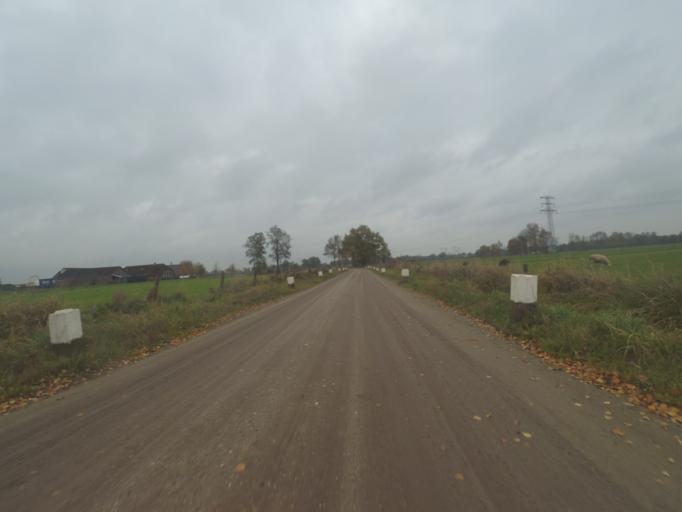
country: NL
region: Gelderland
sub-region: Gemeente Ede
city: Lunteren
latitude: 52.0700
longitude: 5.6141
